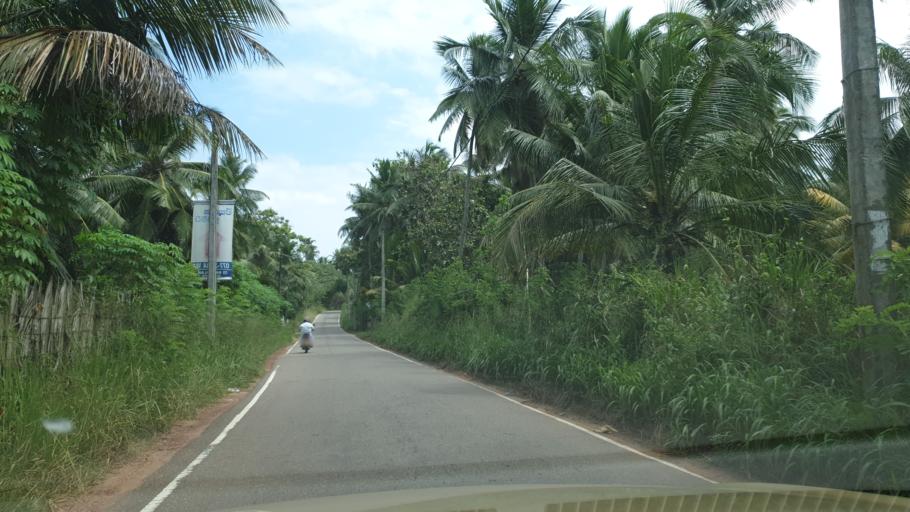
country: LK
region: North Western
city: Kuliyapitiya
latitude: 7.3538
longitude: 79.9696
